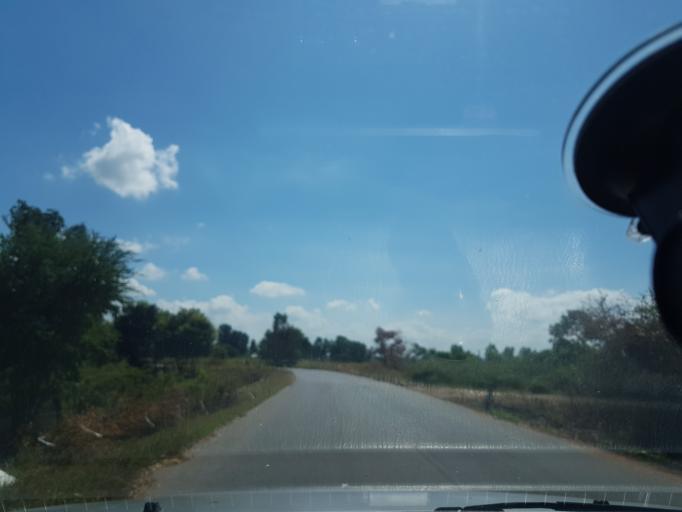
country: TH
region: Lop Buri
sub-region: Amphoe Tha Luang
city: Tha Luang
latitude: 15.0001
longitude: 101.0055
